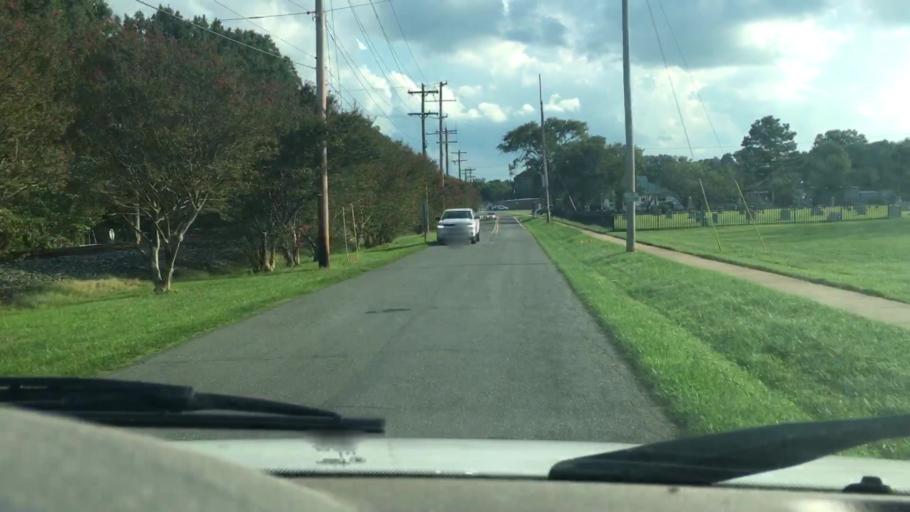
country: US
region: North Carolina
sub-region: Mecklenburg County
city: Huntersville
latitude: 35.4158
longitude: -80.8408
